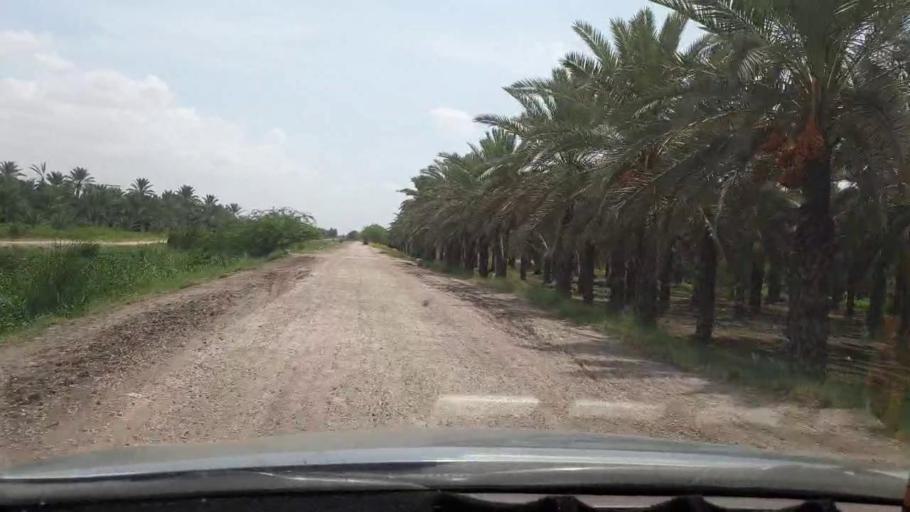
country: PK
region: Sindh
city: Khairpur
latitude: 27.4573
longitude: 68.7906
